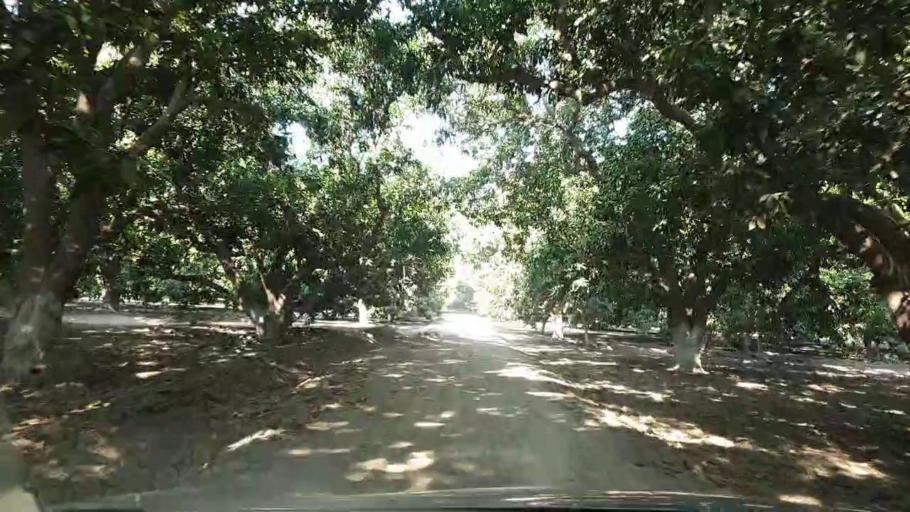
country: PK
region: Sindh
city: Tando Jam
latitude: 25.4682
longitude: 68.6230
